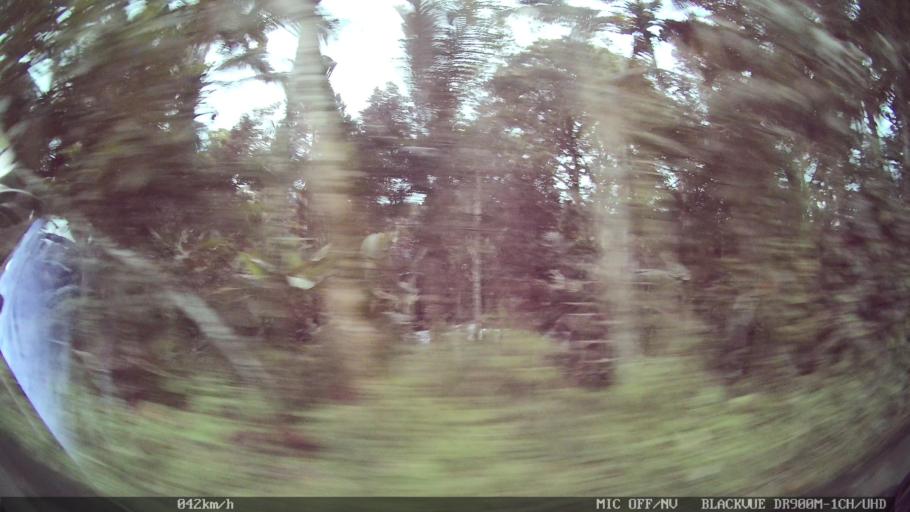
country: ID
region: Bali
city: Peneng
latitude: -8.3563
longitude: 115.2111
